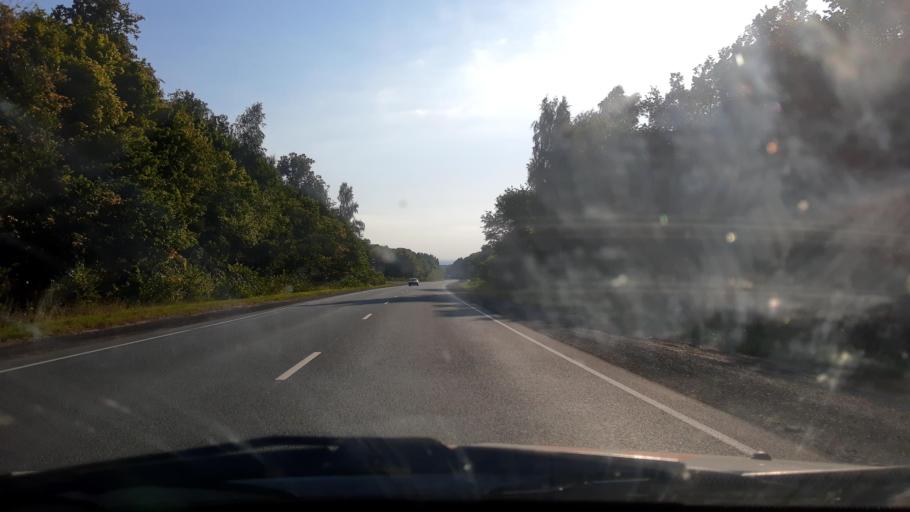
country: RU
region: Bashkortostan
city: Oktyabr'skiy
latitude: 54.4444
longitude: 53.5500
